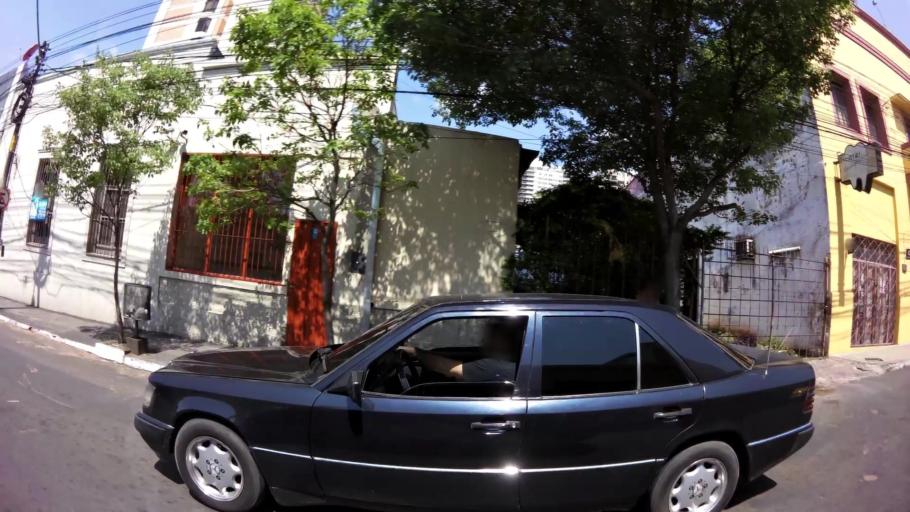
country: PY
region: Asuncion
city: Asuncion
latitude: -25.2881
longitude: -57.6241
